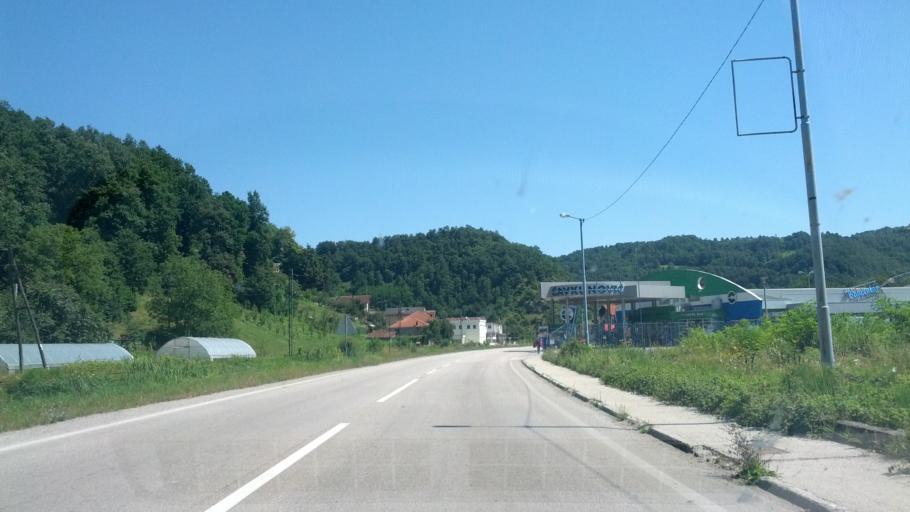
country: BA
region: Federation of Bosnia and Herzegovina
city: Bosanska Krupa
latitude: 44.8964
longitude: 16.1556
